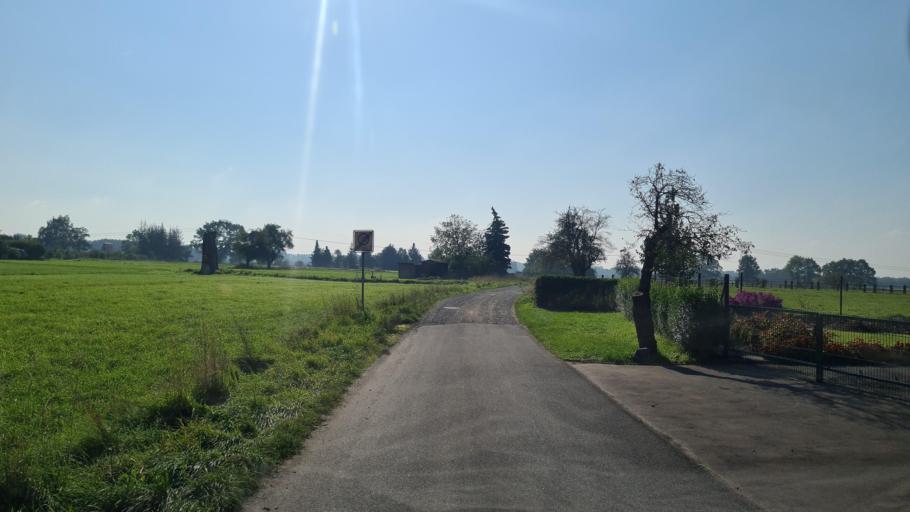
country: DE
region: Brandenburg
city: Luckau
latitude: 51.8459
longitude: 13.7037
